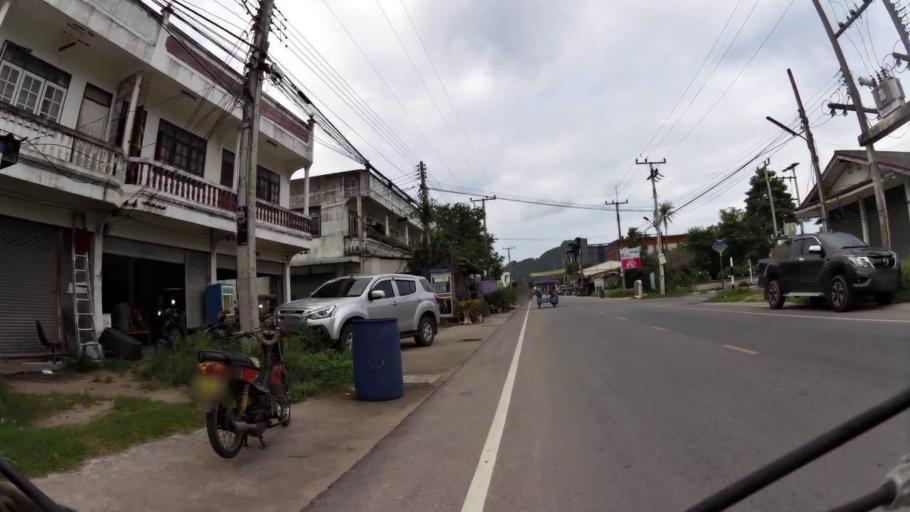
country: TH
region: Prachuap Khiri Khan
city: Prachuap Khiri Khan
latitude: 11.7377
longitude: 99.7799
